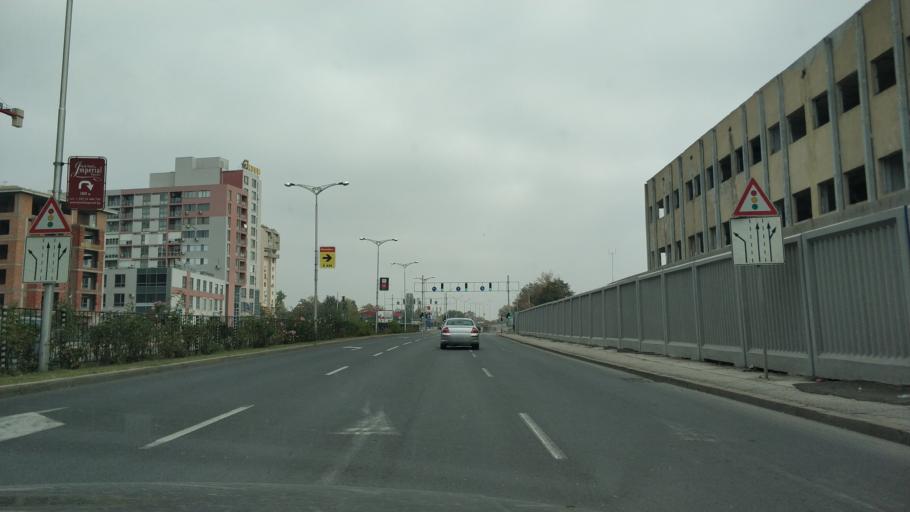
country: BG
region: Plovdiv
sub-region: Obshtina Plovdiv
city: Plovdiv
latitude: 42.1596
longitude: 24.7604
